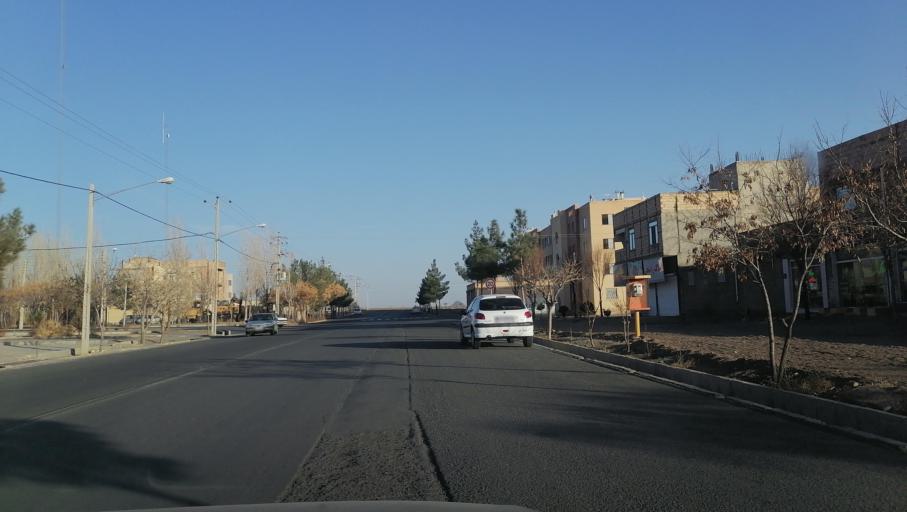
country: IR
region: Razavi Khorasan
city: Sabzevar
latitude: 36.2859
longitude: 57.6800
